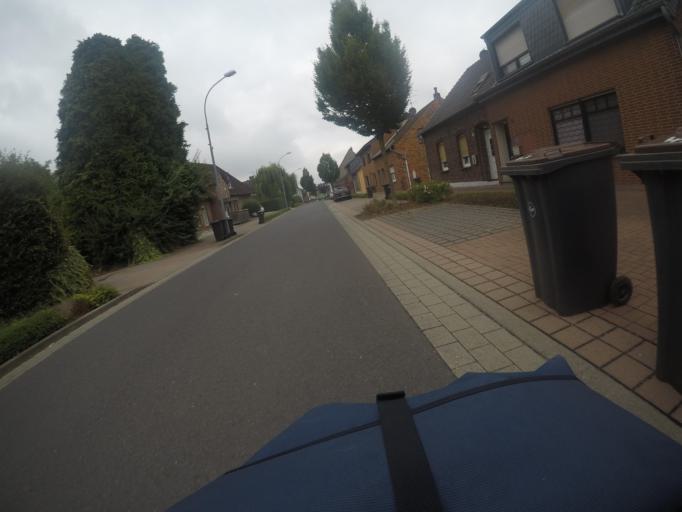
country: DE
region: North Rhine-Westphalia
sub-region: Regierungsbezirk Dusseldorf
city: Wachtendonk
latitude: 51.4538
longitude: 6.3794
